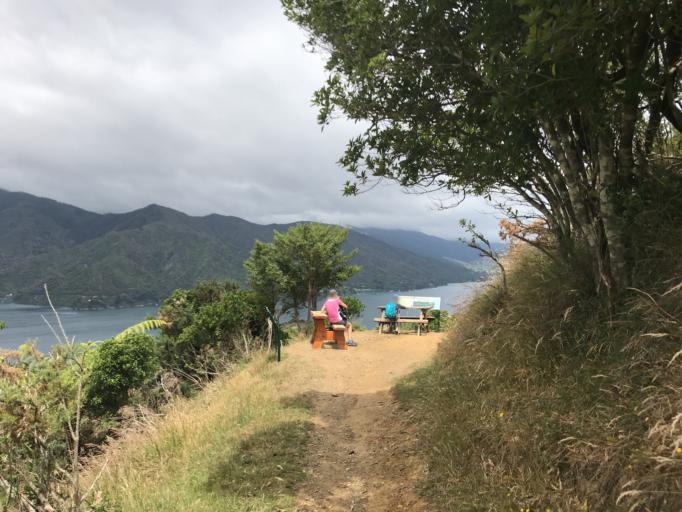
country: NZ
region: Marlborough
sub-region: Marlborough District
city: Picton
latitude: -41.2497
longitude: 173.9626
